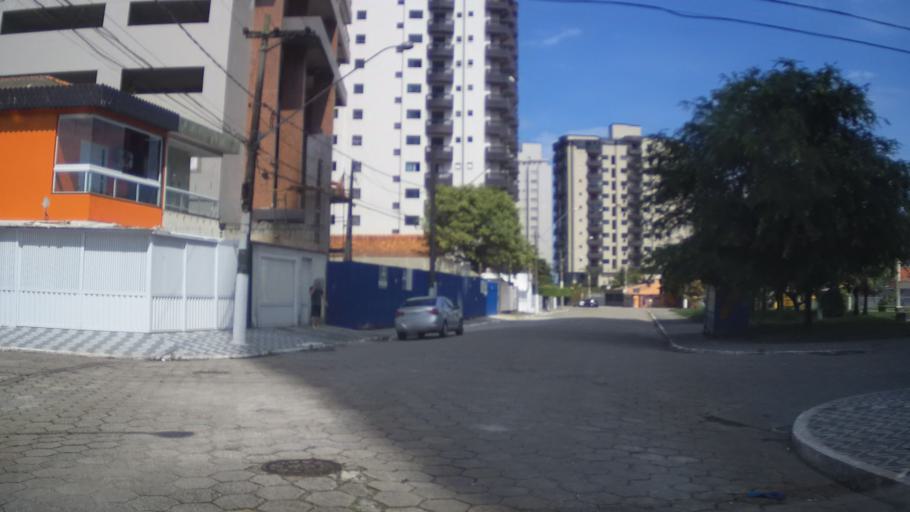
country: BR
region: Sao Paulo
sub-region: Praia Grande
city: Praia Grande
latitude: -24.0126
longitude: -46.4291
